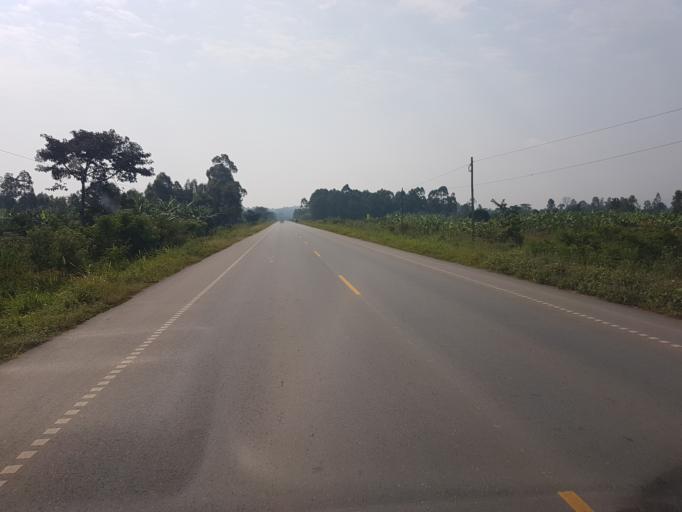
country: UG
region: Western Region
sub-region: Mbarara District
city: Bwizibwera
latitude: -0.6427
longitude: 30.5681
